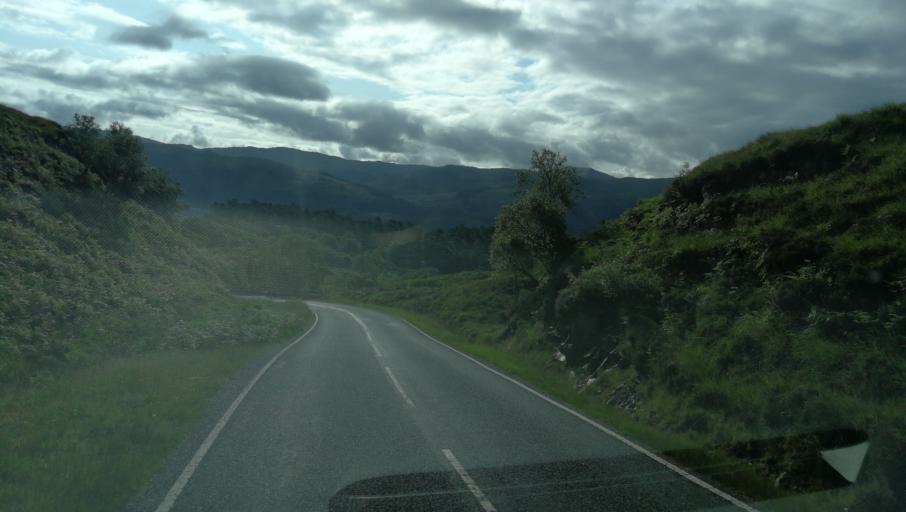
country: GB
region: Scotland
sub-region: Argyll and Bute
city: Isle Of Mull
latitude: 56.6787
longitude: -5.8466
